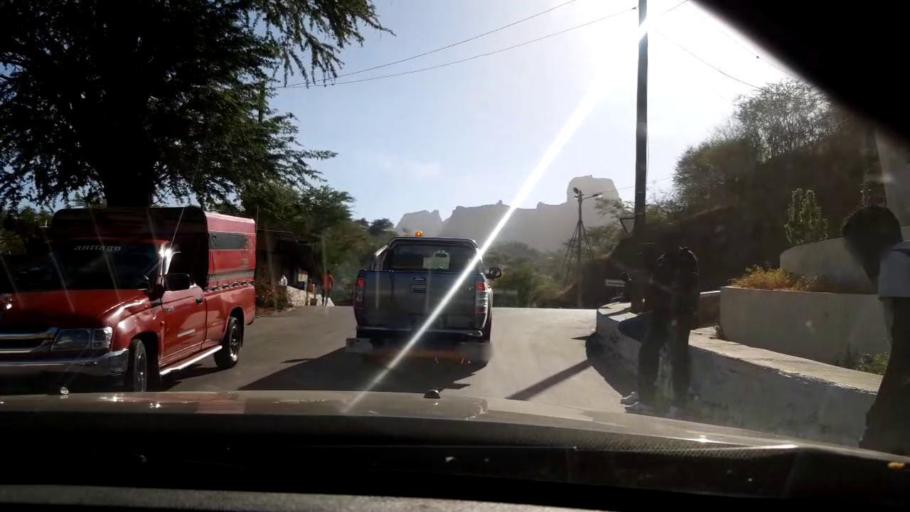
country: CV
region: Sao Lourenco dos Orgaos
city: Joao Teves
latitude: 15.0679
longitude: -23.5805
